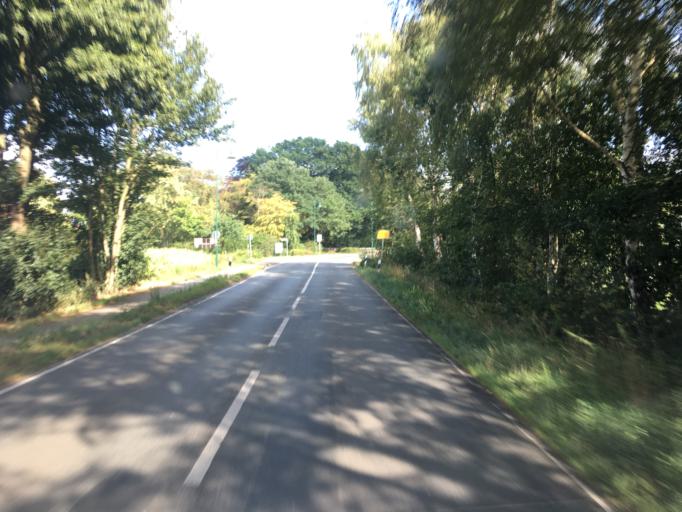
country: DE
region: Lower Saxony
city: Wardenburg
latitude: 53.0672
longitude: 8.1852
